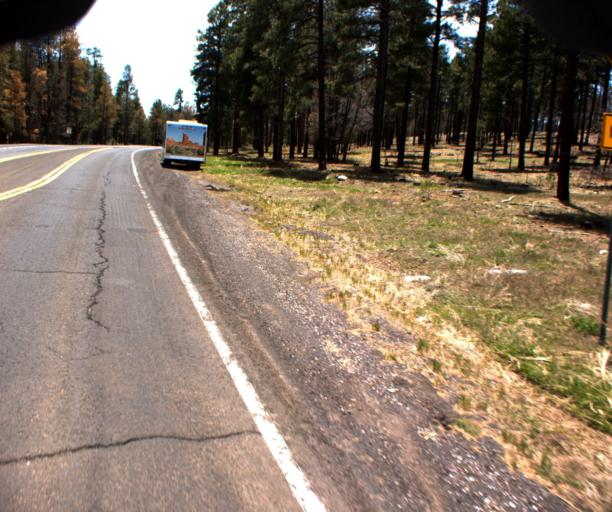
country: US
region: Arizona
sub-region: Coconino County
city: Kachina Village
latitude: 35.0381
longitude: -111.7334
